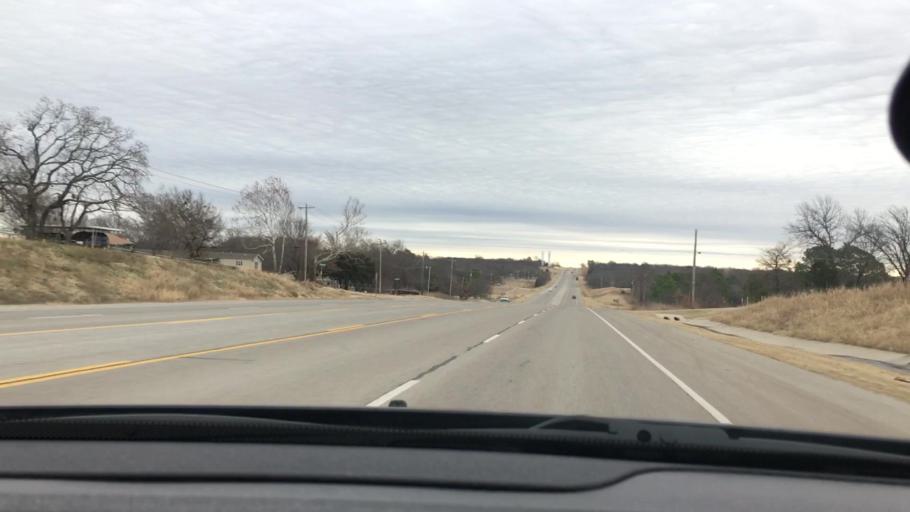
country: US
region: Oklahoma
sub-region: Carter County
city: Dickson
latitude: 34.1871
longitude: -97.0178
